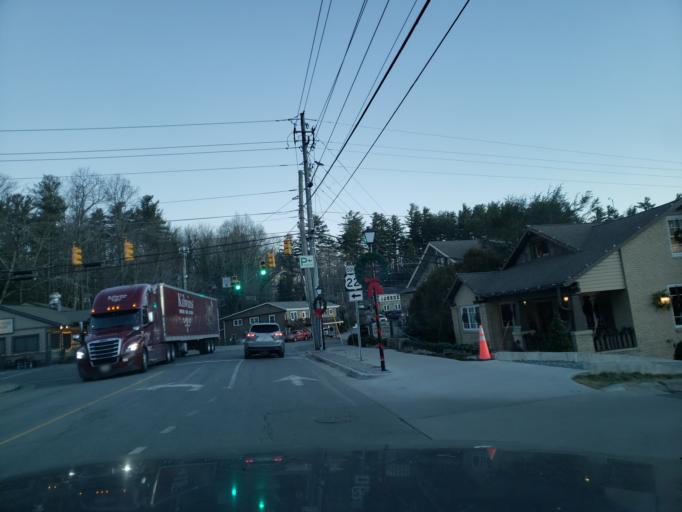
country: US
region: North Carolina
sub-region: Watauga County
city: Blowing Rock
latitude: 36.1347
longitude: -81.6779
